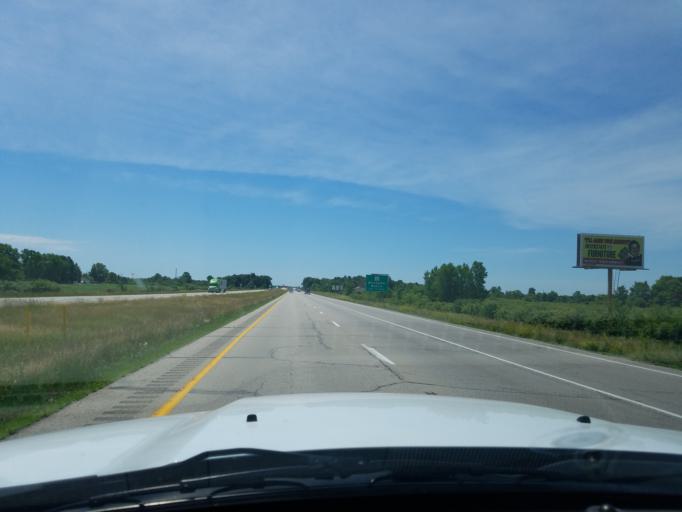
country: US
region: Indiana
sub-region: Delaware County
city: Muncie
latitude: 40.2066
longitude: -85.3361
